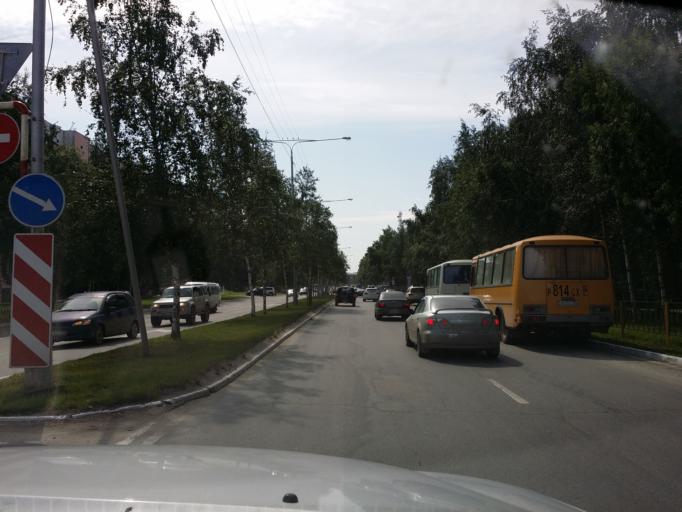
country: RU
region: Khanty-Mansiyskiy Avtonomnyy Okrug
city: Nizhnevartovsk
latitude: 60.9453
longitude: 76.5662
